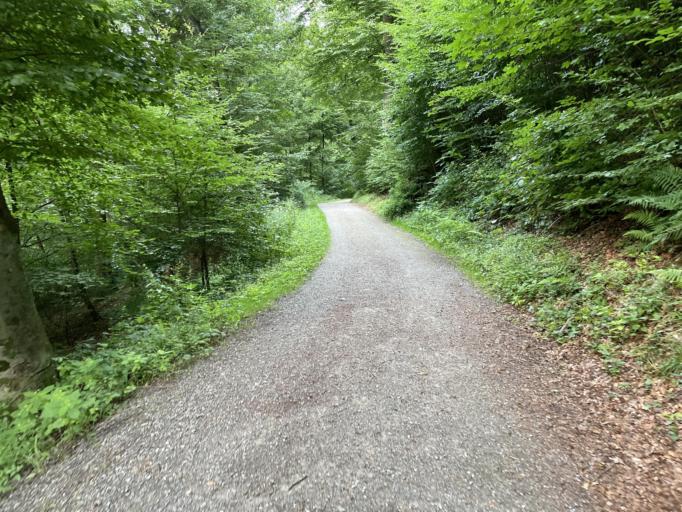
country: DE
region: North Rhine-Westphalia
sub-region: Regierungsbezirk Dusseldorf
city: Essen
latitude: 51.4191
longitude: 7.0541
